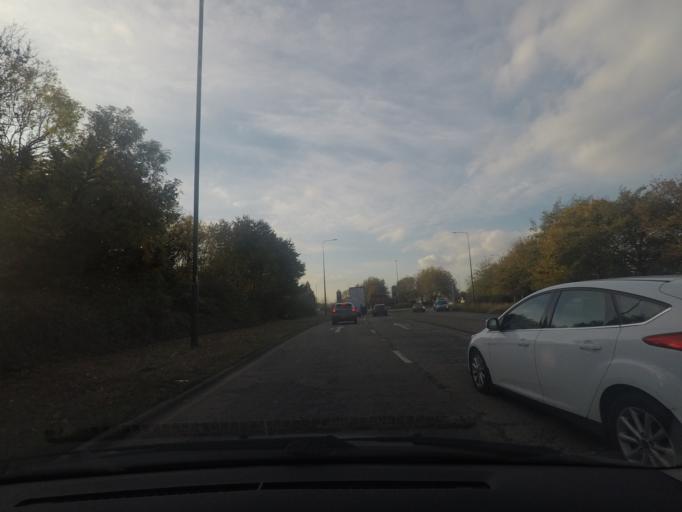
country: GB
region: England
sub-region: North East Lincolnshire
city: Grimbsy
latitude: 53.5744
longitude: -0.0950
